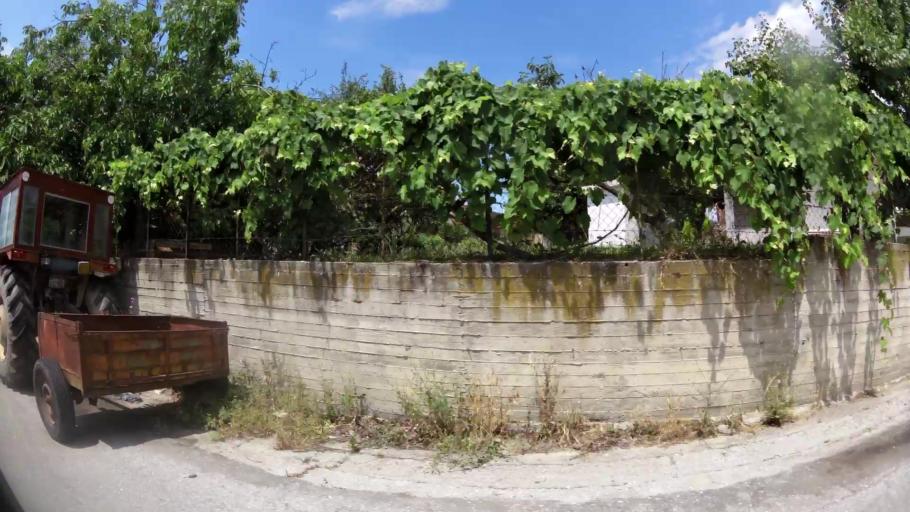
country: GR
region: Central Macedonia
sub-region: Nomos Pierias
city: Katerini
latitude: 40.2623
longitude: 22.5000
